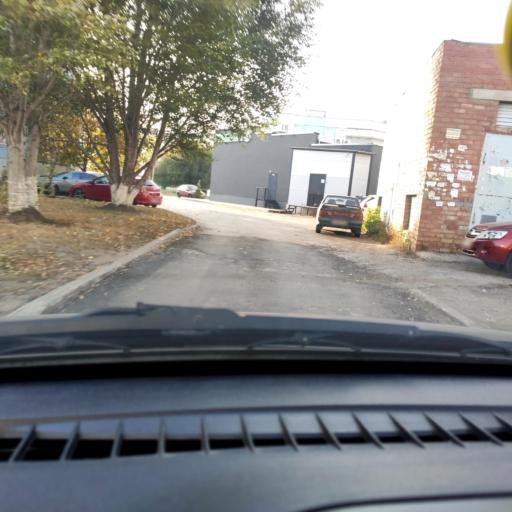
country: RU
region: Samara
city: Tol'yatti
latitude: 53.5476
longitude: 49.3368
